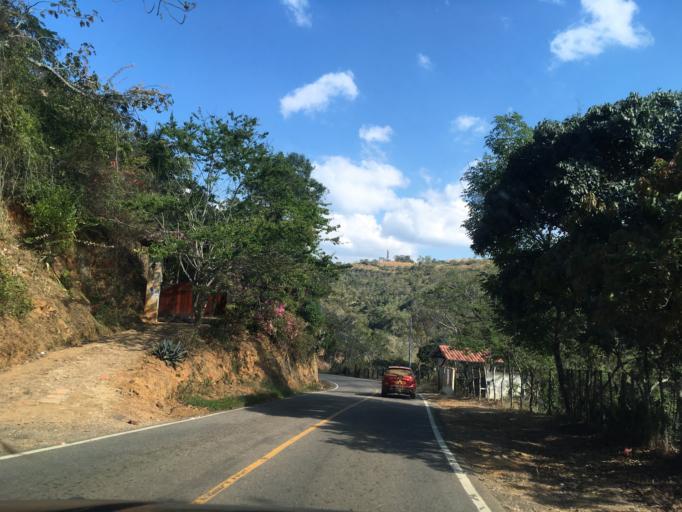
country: CO
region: Santander
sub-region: San Gil
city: San Gil
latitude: 6.6003
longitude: -73.1563
